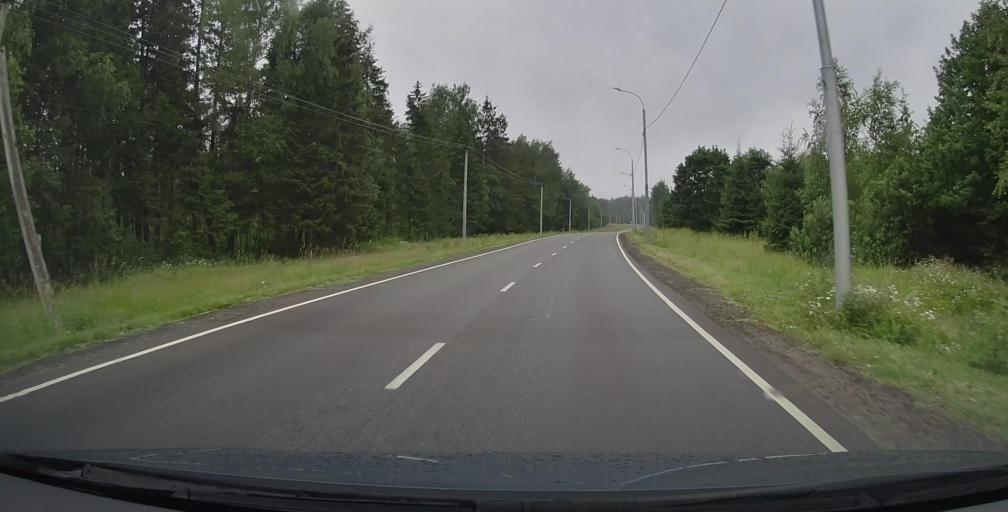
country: RU
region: Moskovskaya
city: Selyatino
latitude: 55.4210
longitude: 36.9985
